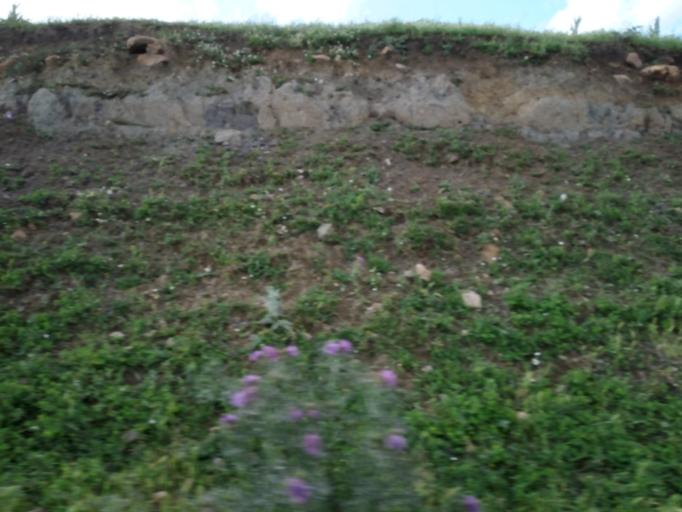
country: DZ
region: Tipaza
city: Hadjout
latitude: 36.3729
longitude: 2.4905
